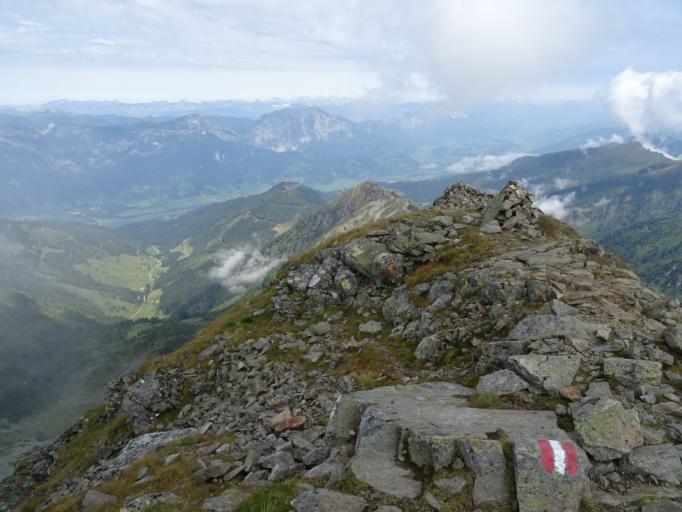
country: AT
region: Styria
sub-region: Politischer Bezirk Liezen
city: Haus
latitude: 47.3469
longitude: 13.7911
